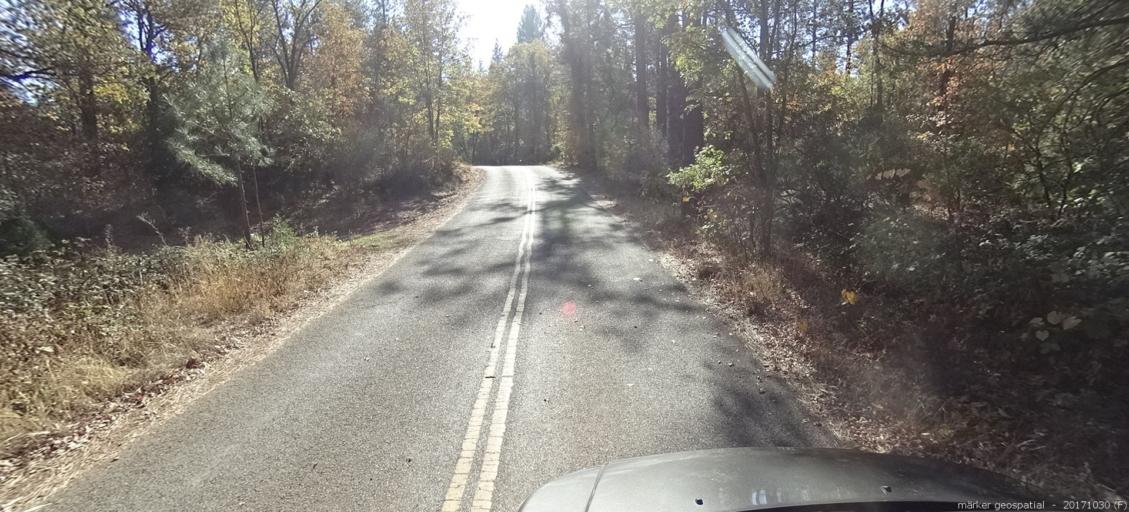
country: US
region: California
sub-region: Shasta County
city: Shingletown
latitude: 40.6056
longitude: -121.9562
